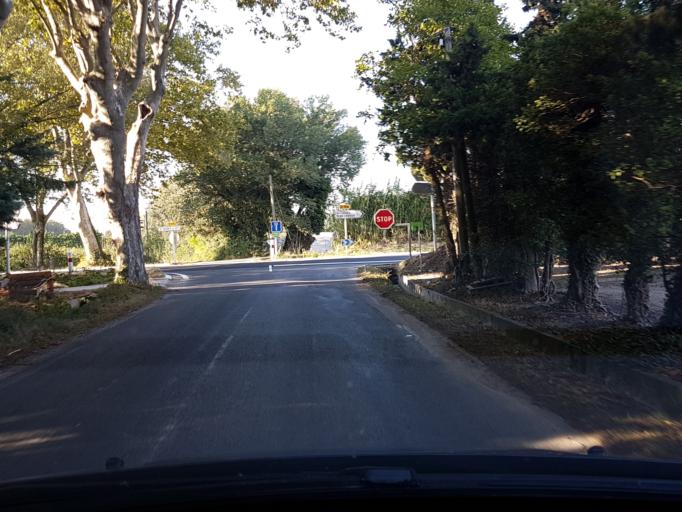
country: FR
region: Provence-Alpes-Cote d'Azur
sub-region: Departement des Bouches-du-Rhone
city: Molleges
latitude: 43.7849
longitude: 4.9268
